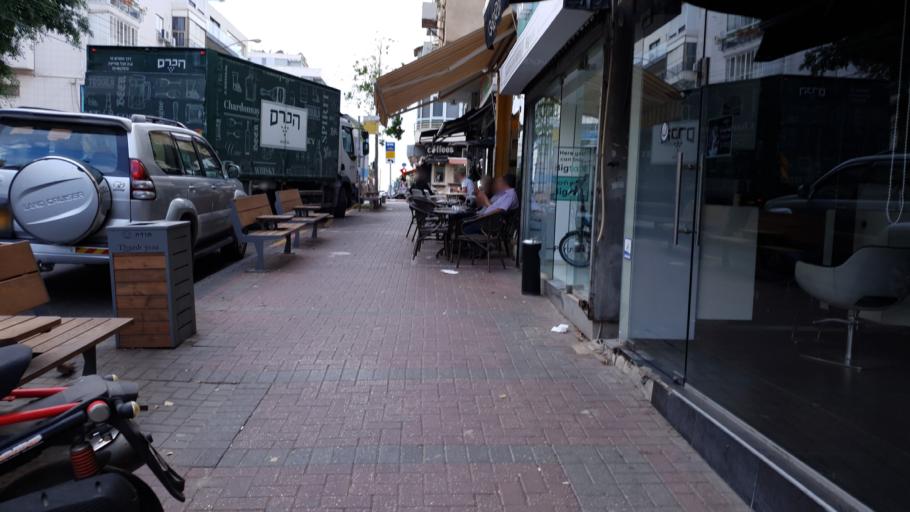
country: IL
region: Tel Aviv
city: Tel Aviv
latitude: 32.0771
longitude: 34.7692
